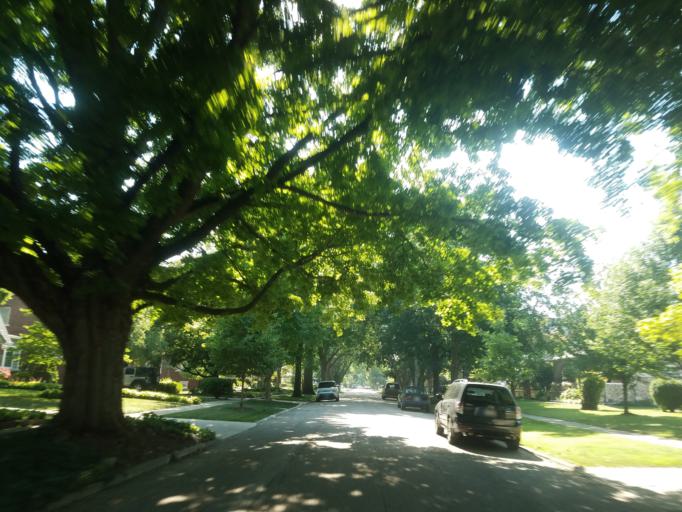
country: US
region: Illinois
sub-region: McLean County
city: Bloomington
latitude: 40.4754
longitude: -88.9657
